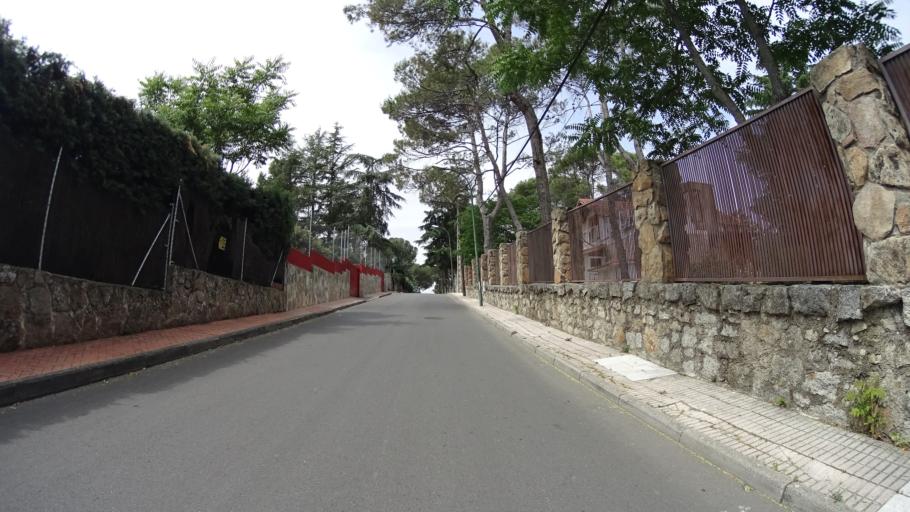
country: ES
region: Madrid
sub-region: Provincia de Madrid
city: Galapagar
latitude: 40.5720
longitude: -4.0009
